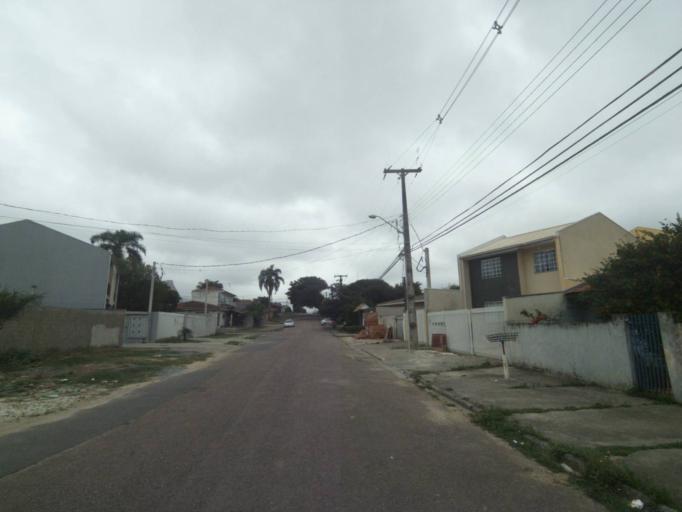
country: BR
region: Parana
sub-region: Sao Jose Dos Pinhais
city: Sao Jose dos Pinhais
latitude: -25.5442
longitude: -49.2774
